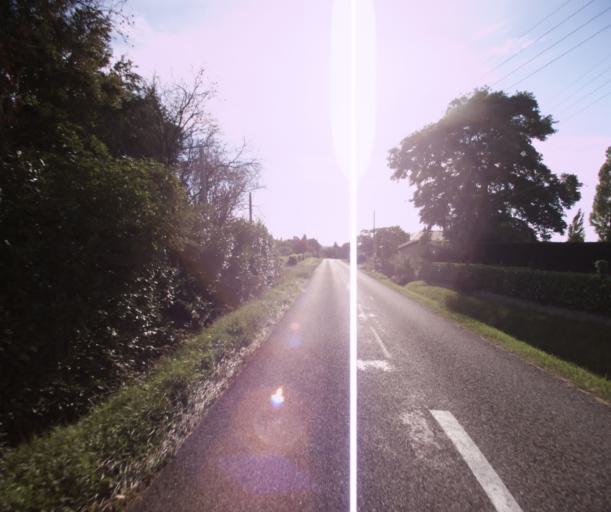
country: FR
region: Midi-Pyrenees
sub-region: Departement du Gers
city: Eauze
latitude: 43.8593
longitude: 0.0589
